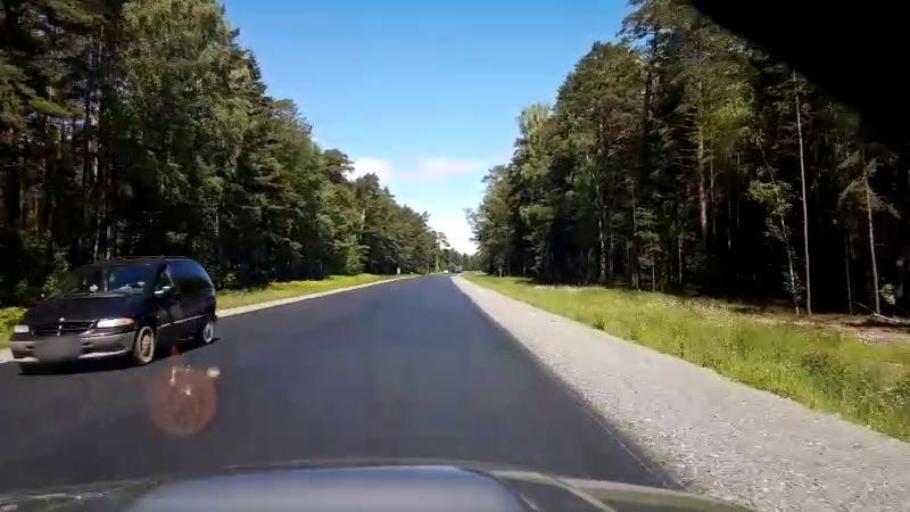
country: LV
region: Salacgrivas
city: Ainazi
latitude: 57.8269
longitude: 24.3450
